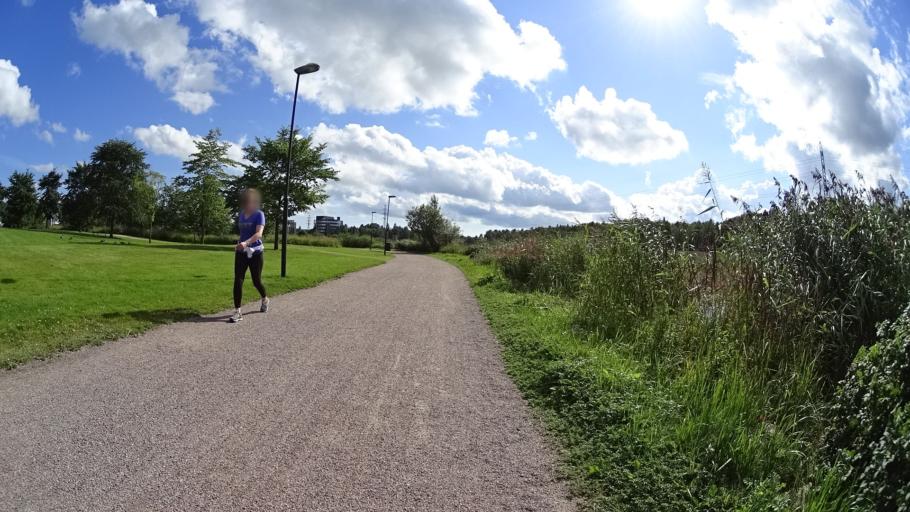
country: FI
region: Uusimaa
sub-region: Helsinki
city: Helsinki
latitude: 60.2000
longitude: 24.8920
